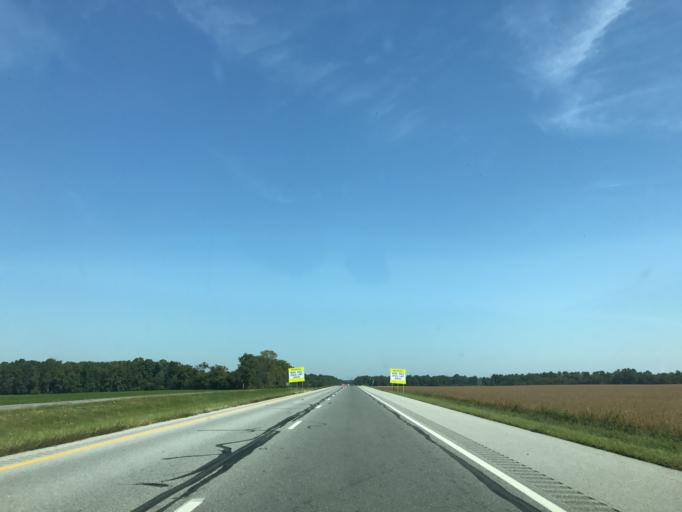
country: US
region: Delaware
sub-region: New Castle County
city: Middletown
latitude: 39.3943
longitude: -75.7890
